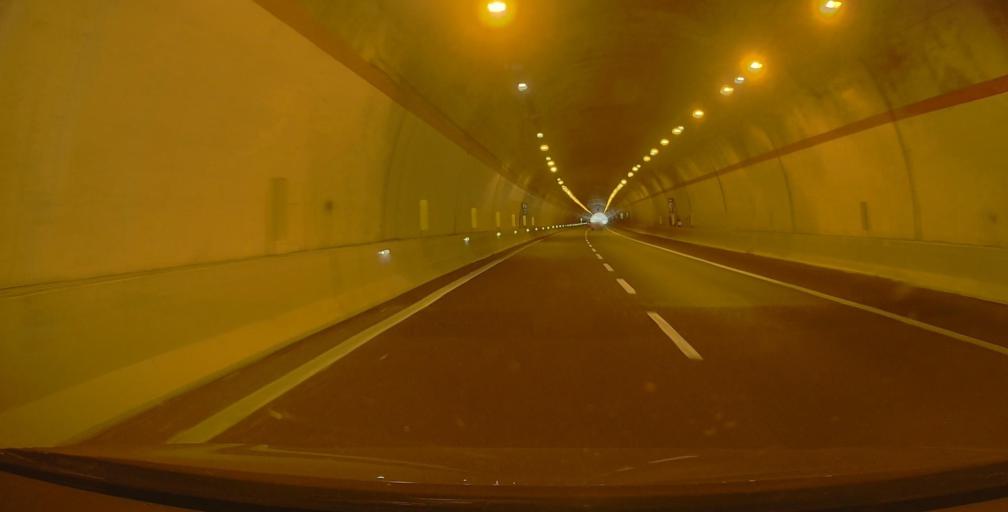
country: IT
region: Calabria
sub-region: Provincia di Cosenza
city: Laino Castello-Nuovo Centro
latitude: 39.9297
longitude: 15.9643
